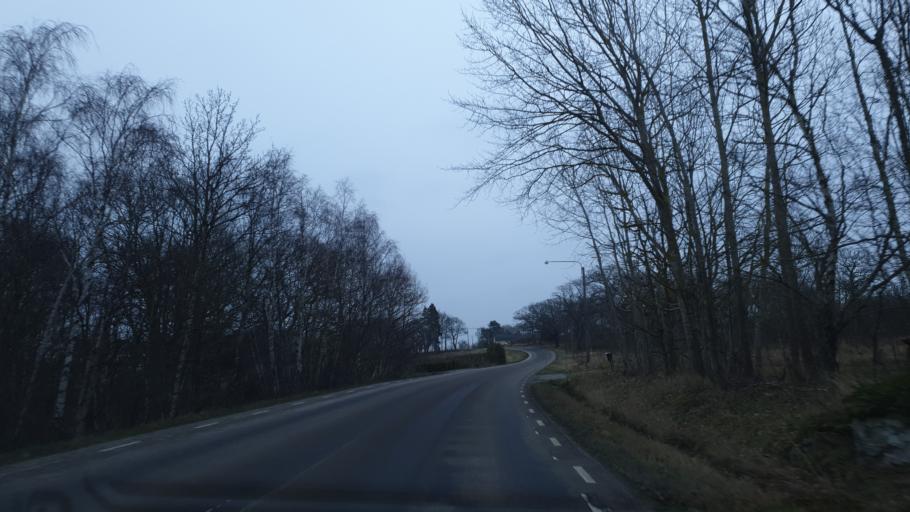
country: SE
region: Blekinge
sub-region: Karlskrona Kommun
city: Sturko
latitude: 56.1108
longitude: 15.7136
